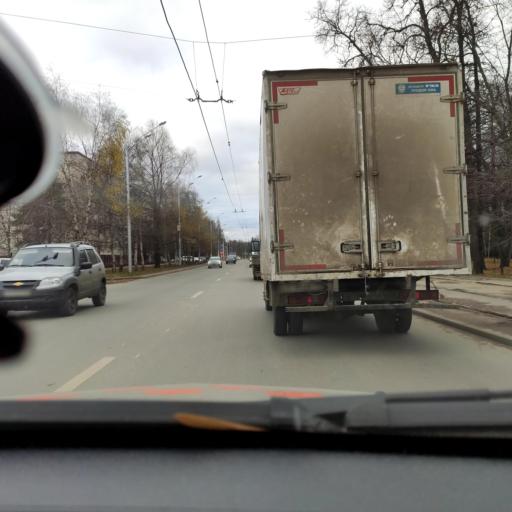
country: RU
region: Bashkortostan
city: Ufa
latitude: 54.7657
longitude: 56.0085
